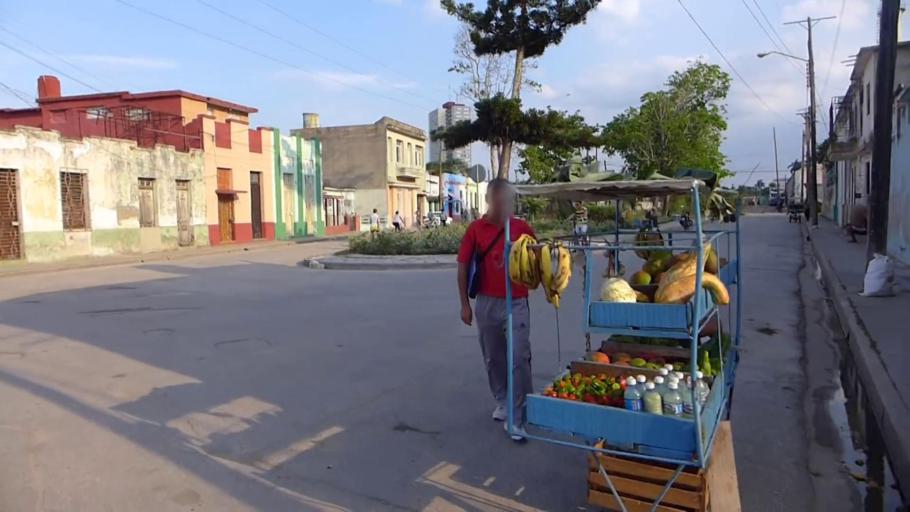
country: CU
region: Camaguey
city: Camaguey
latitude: 21.3840
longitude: -77.9080
